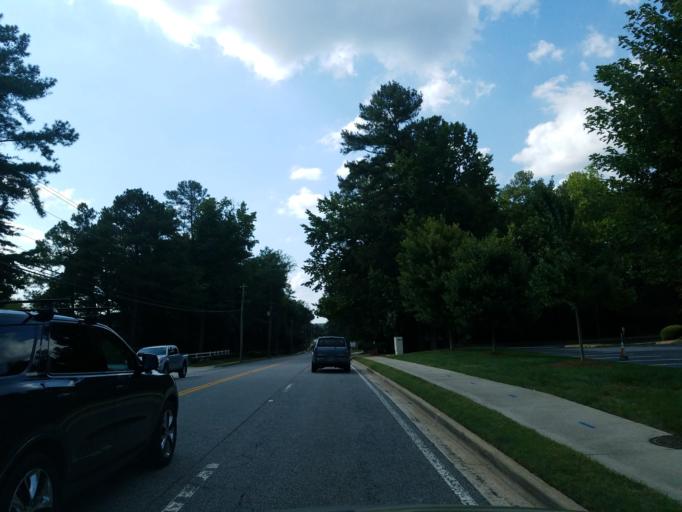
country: US
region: Georgia
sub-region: Fulton County
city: Roswell
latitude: 33.9912
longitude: -84.3446
